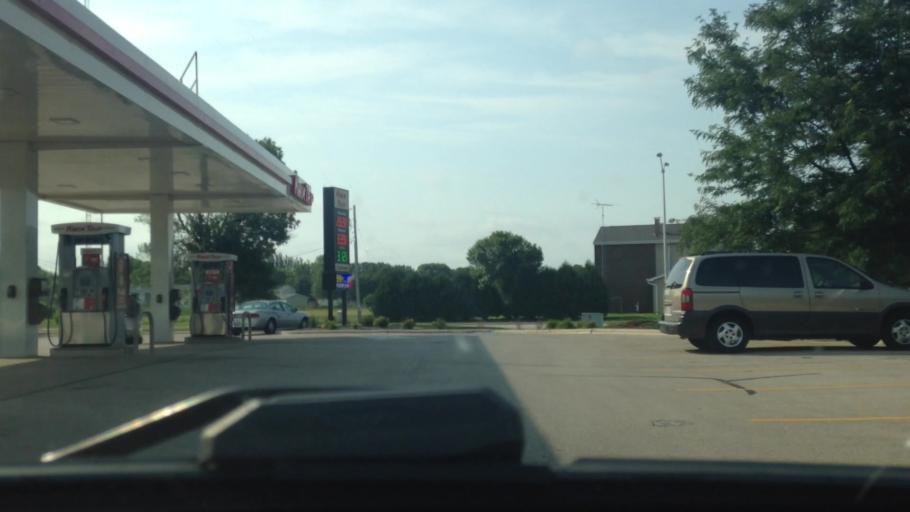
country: US
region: Wisconsin
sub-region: Fond du Lac County
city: North Fond du Lac
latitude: 43.7923
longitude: -88.4730
